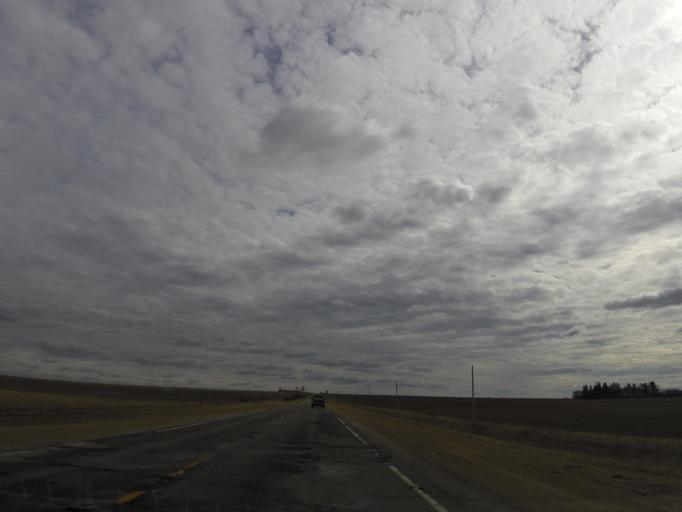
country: US
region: Iowa
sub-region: Howard County
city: Cresco
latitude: 43.3347
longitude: -92.2987
